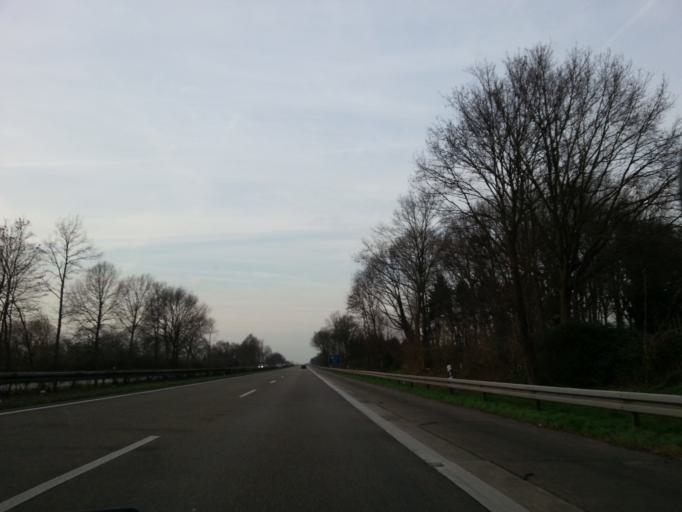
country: DE
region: North Rhine-Westphalia
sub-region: Regierungsbezirk Munster
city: Isselburg
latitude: 51.8116
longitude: 6.4582
